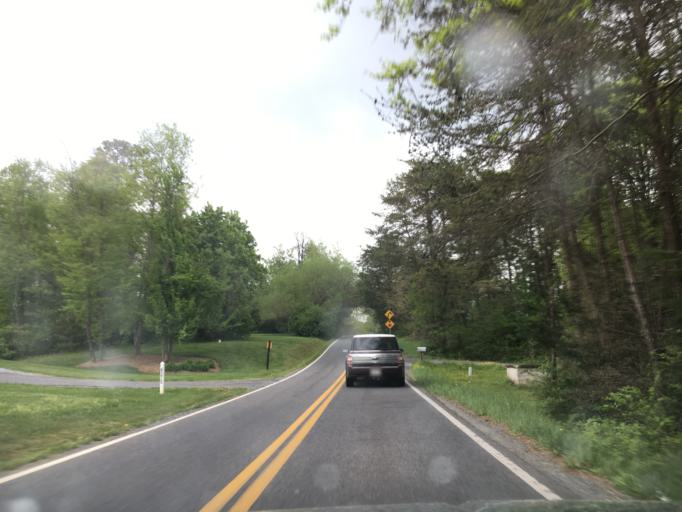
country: US
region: Virginia
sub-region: Campbell County
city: Rustburg
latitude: 37.3324
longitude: -79.1084
